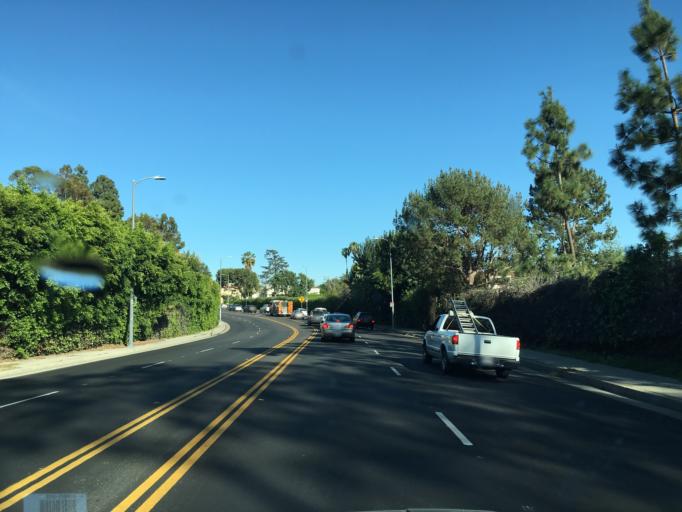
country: US
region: California
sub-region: Los Angeles County
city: Hollywood
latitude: 34.0758
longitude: -118.3294
